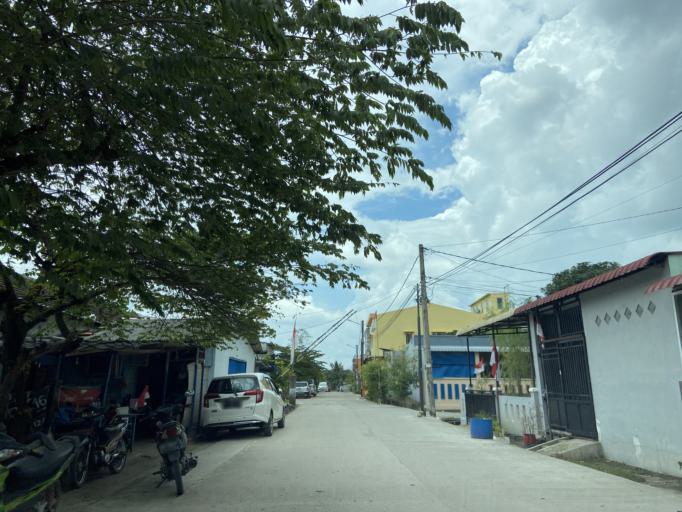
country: SG
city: Singapore
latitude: 1.1262
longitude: 104.0143
